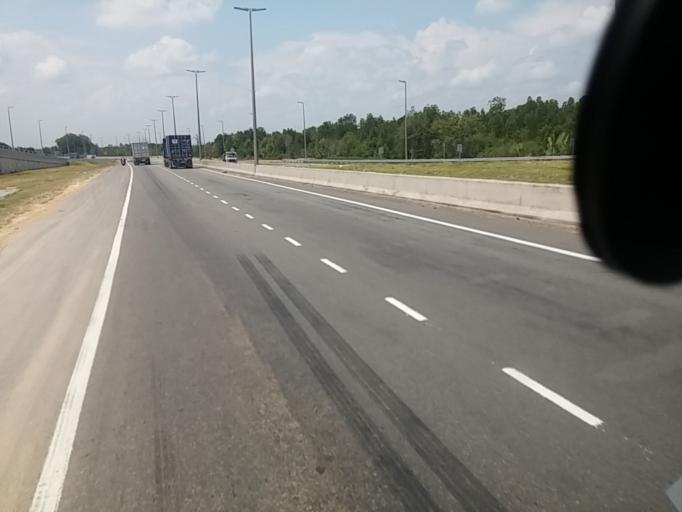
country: MY
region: Selangor
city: Klang
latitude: 2.9614
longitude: 101.3518
